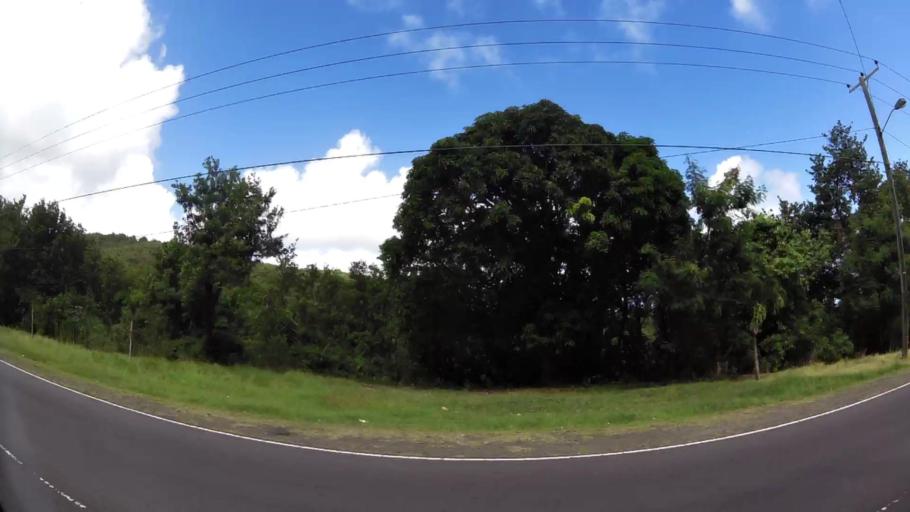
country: LC
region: Dennery Quarter
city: Dennery
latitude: 13.9204
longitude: -60.8969
